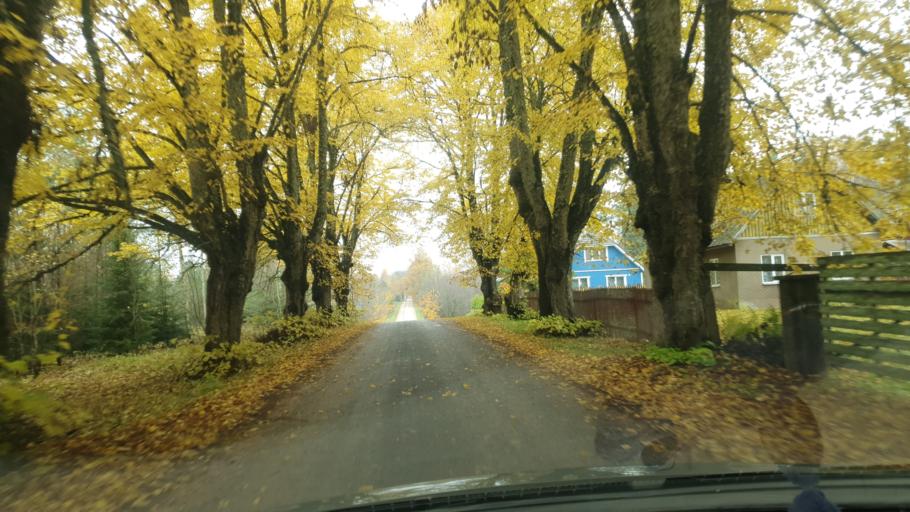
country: EE
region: Viljandimaa
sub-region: Karksi vald
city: Karksi-Nuia
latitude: 57.9956
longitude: 25.6648
